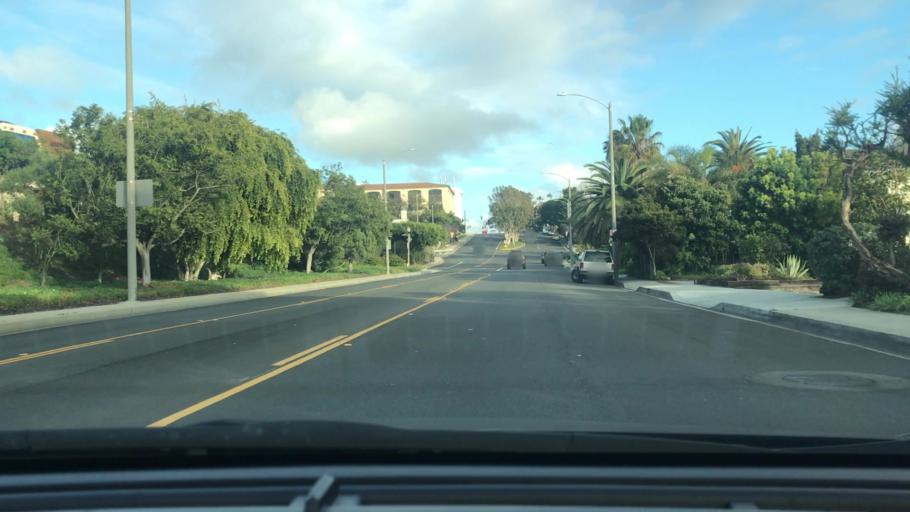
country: US
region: California
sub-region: Los Angeles County
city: Hermosa Beach
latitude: 33.8741
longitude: -118.3989
